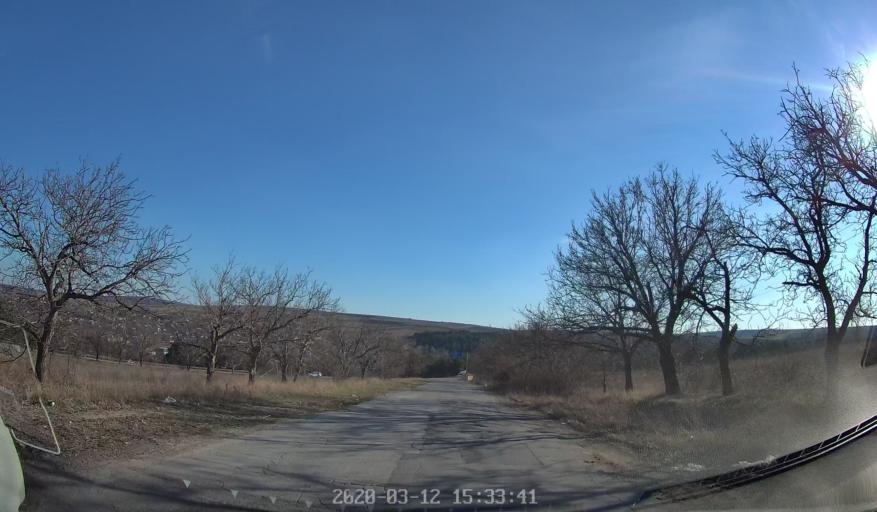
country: MD
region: Chisinau
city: Ciorescu
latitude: 47.1407
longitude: 28.9377
